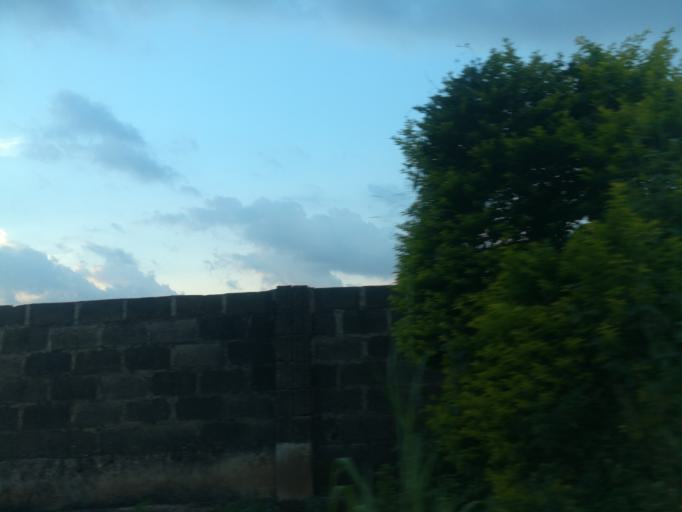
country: NG
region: Oyo
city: Ibadan
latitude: 7.4369
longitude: 3.9302
